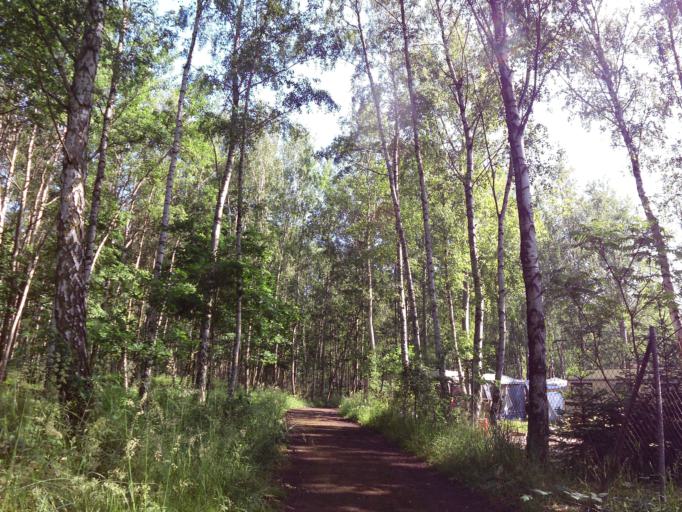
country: CZ
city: Hradek nad Nisou
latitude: 50.8647
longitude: 14.8249
